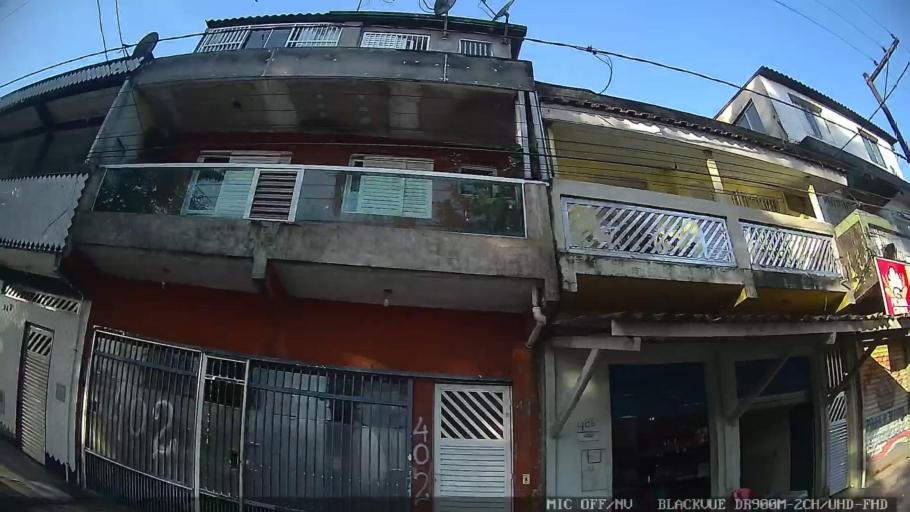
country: BR
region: Sao Paulo
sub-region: Guaruja
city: Guaruja
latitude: -23.9600
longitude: -46.2506
